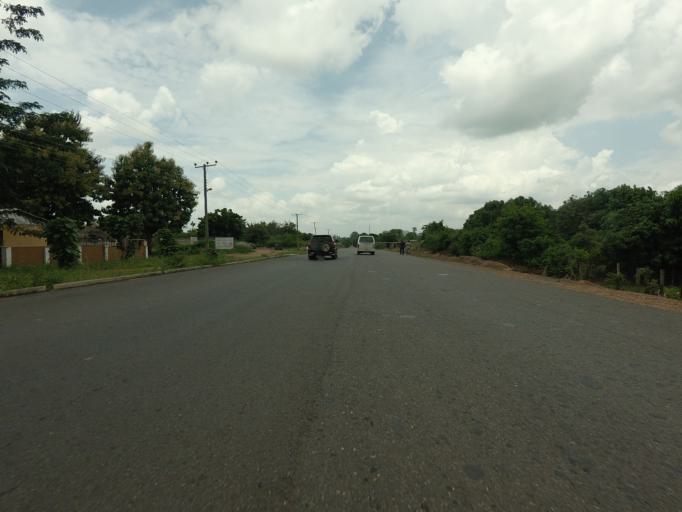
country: GH
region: Volta
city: Ho
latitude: 6.4190
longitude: 0.1721
